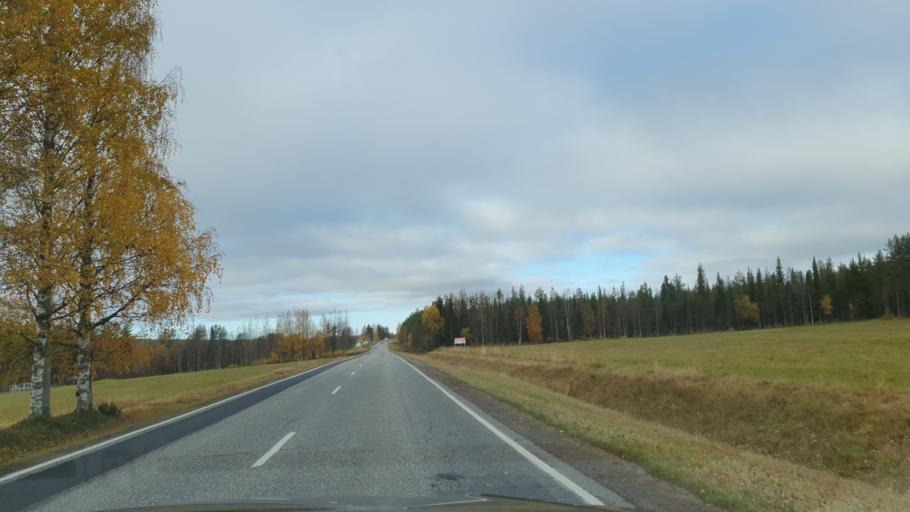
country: FI
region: Lapland
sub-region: Tunturi-Lappi
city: Kittilae
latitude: 67.1517
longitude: 24.9863
